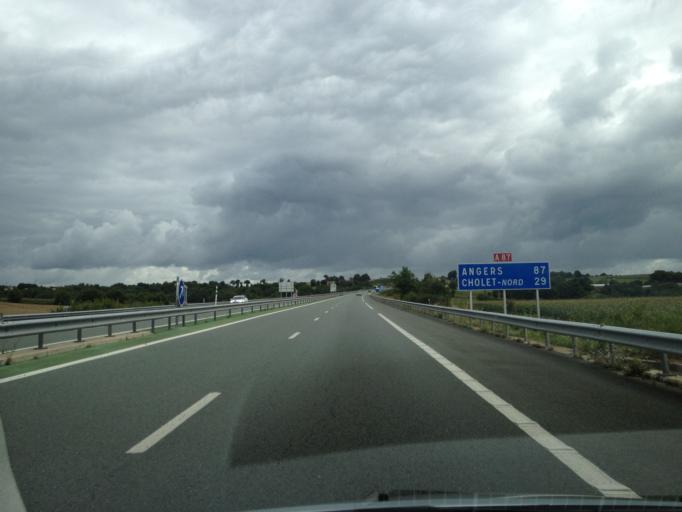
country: FR
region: Pays de la Loire
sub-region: Departement de la Vendee
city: La Gaubretiere
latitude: 46.9115
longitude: -1.0451
